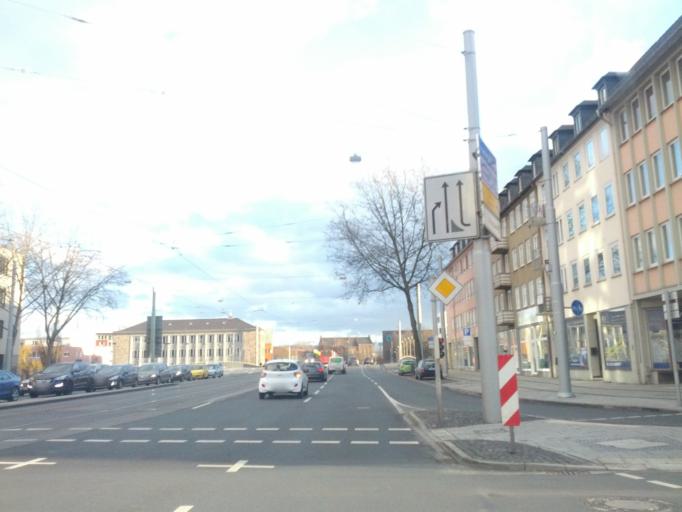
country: DE
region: Hesse
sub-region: Regierungsbezirk Kassel
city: Kassel
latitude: 51.3158
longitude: 9.5052
